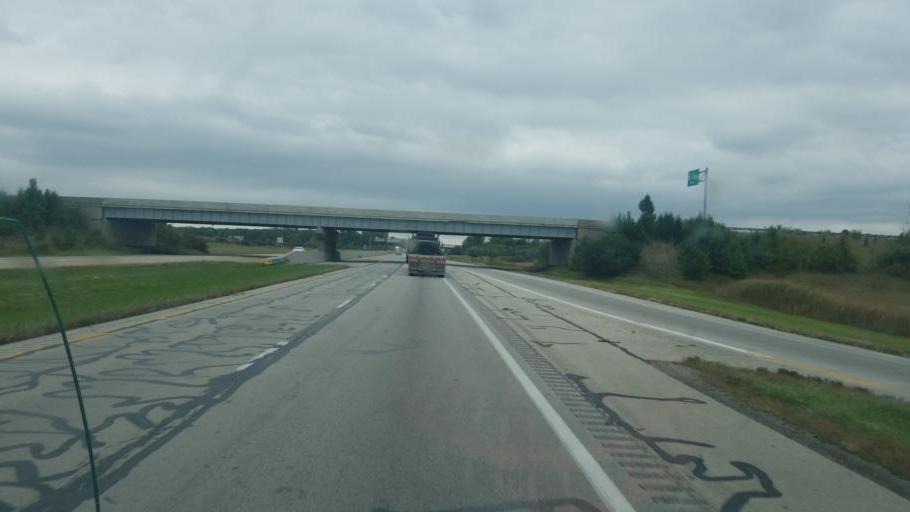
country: US
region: Ohio
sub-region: Lucas County
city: Waterville
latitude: 41.5400
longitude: -83.7043
